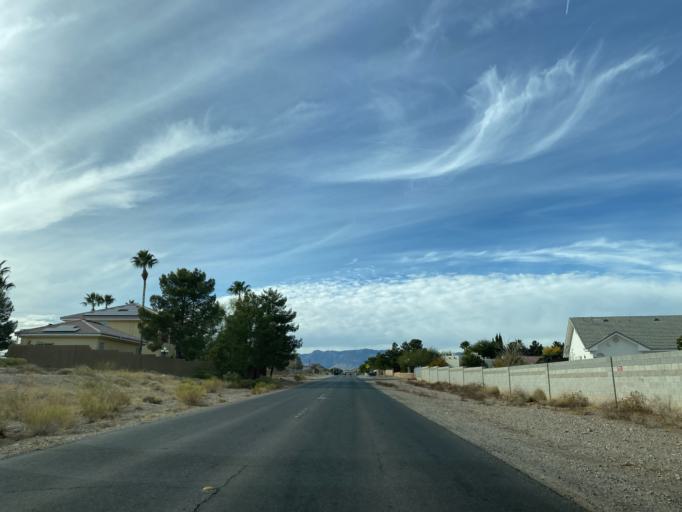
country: US
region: Nevada
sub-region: Clark County
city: Enterprise
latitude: 36.0336
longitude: -115.2732
